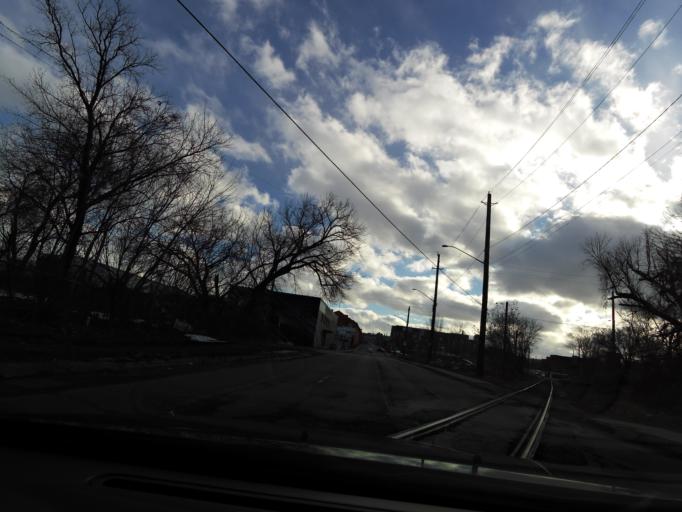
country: CA
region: Ontario
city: Hamilton
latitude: 43.2669
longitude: -79.8536
